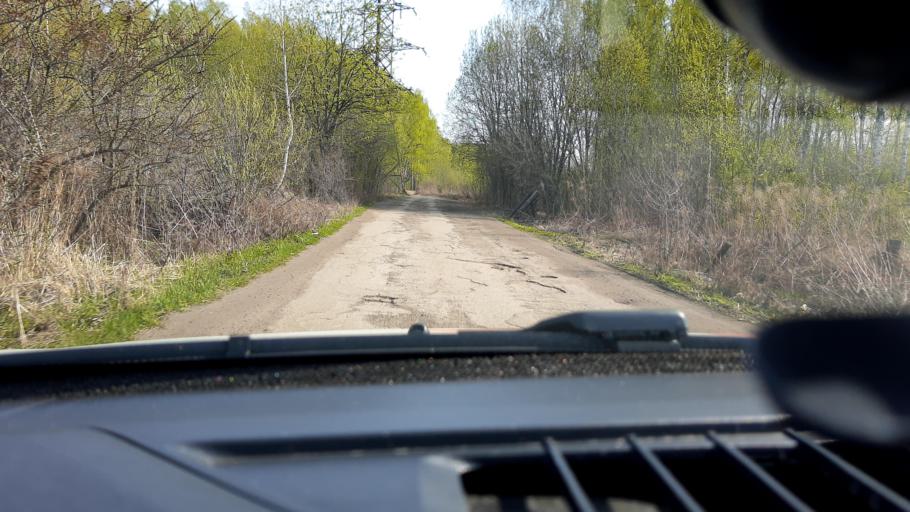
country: RU
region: Nizjnij Novgorod
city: Gorbatovka
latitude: 56.2806
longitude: 43.7980
